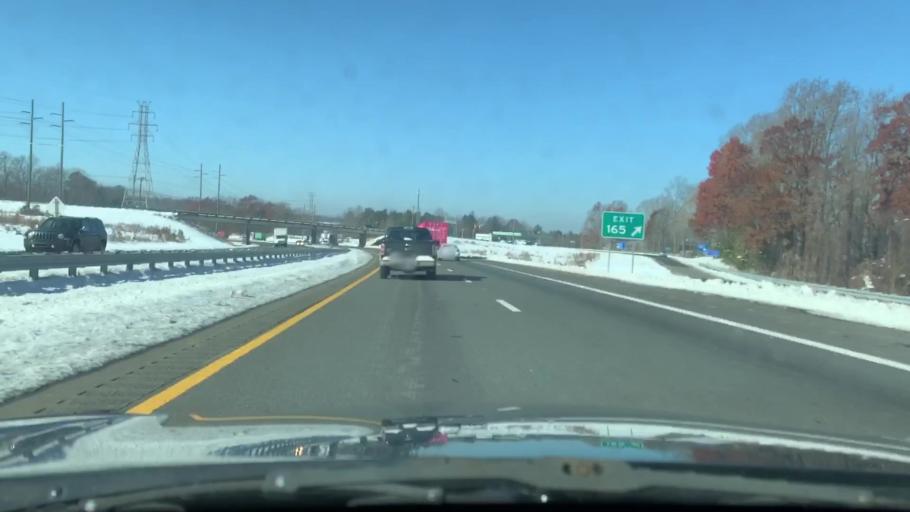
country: US
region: North Carolina
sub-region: Orange County
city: Hillsborough
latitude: 36.0585
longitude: -79.0801
